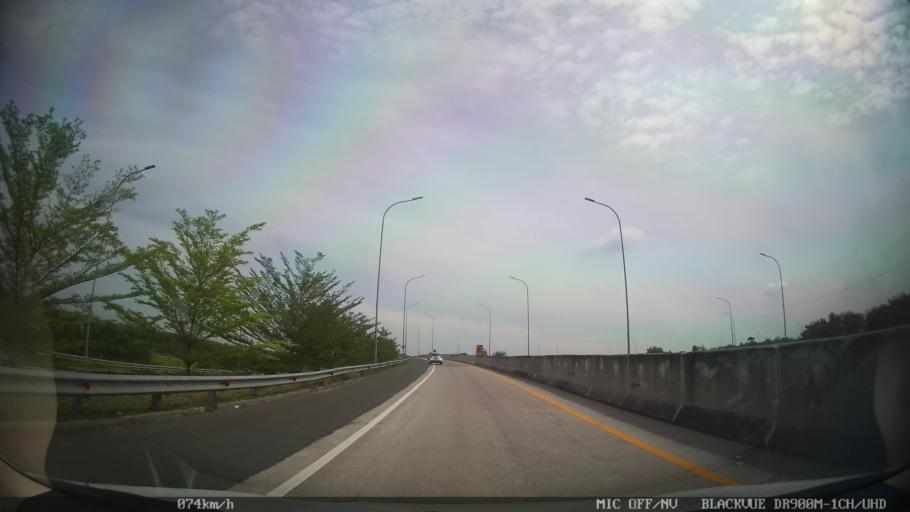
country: ID
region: North Sumatra
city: Medan
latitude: 3.6358
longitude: 98.6366
